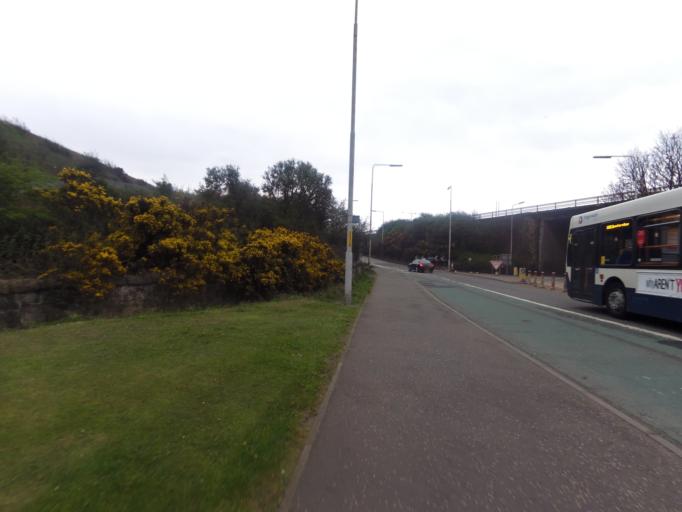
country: GB
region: Scotland
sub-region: Fife
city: Inverkeithing
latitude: 56.0216
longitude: -3.4060
